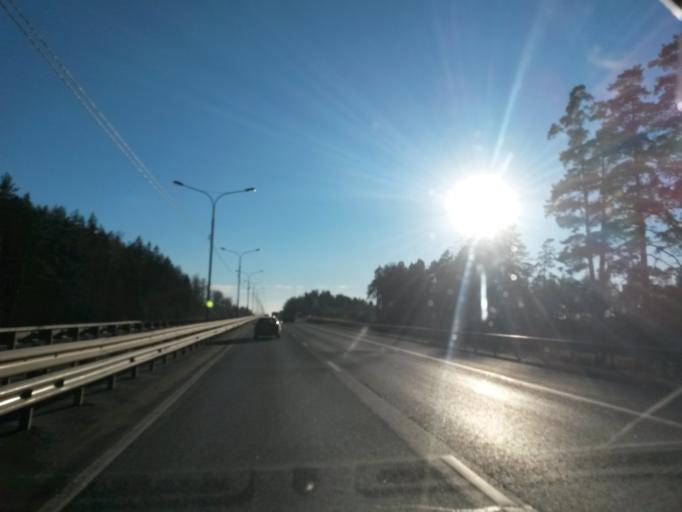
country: RU
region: Moskovskaya
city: Lesnoy
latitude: 56.0692
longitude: 37.9039
